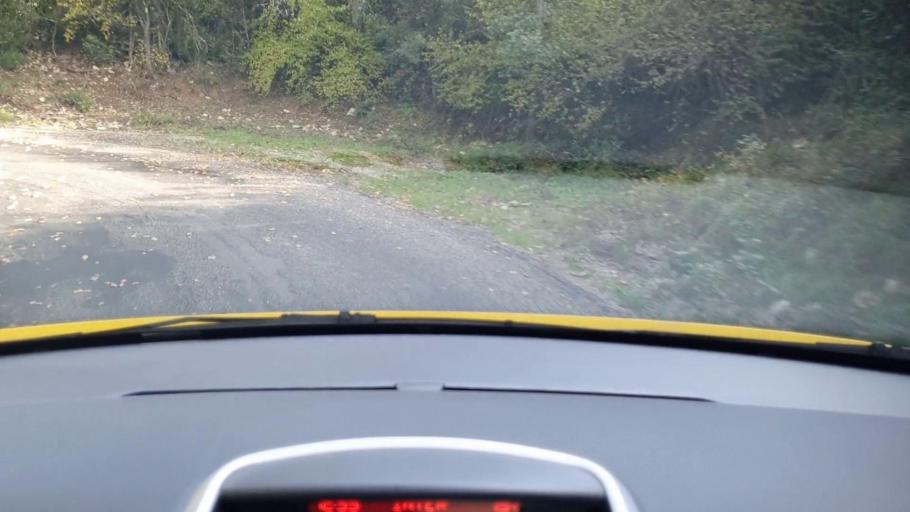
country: FR
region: Languedoc-Roussillon
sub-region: Departement du Gard
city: Lasalle
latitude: 44.0369
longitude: 3.9210
